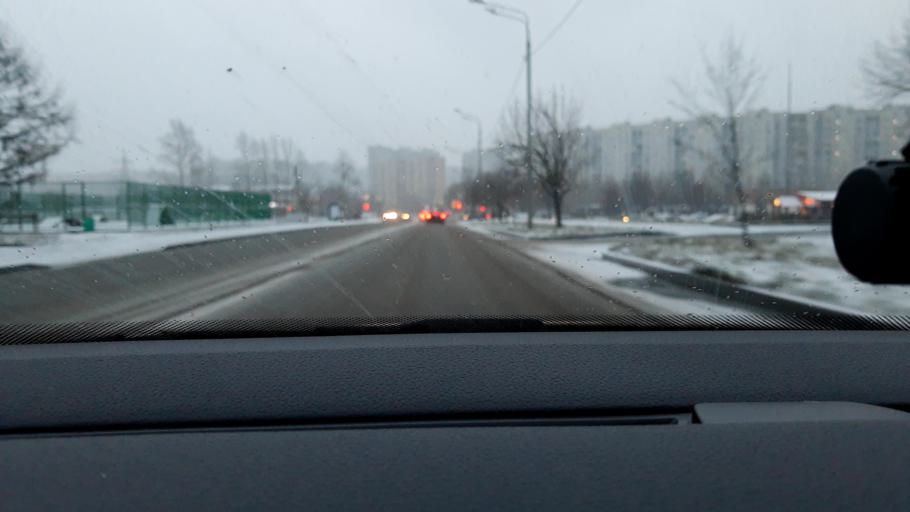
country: RU
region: Moscow
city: Mar'ino
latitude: 55.6542
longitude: 37.7184
